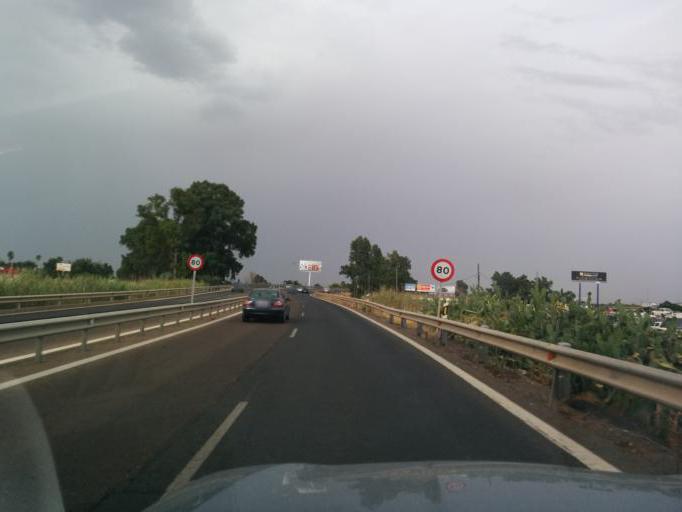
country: ES
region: Andalusia
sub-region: Provincia de Sevilla
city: Sevilla
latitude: 37.4141
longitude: -5.9361
